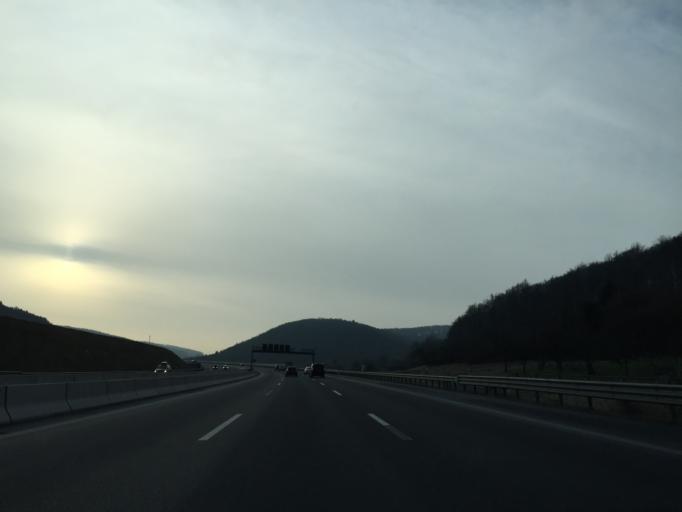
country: DE
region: Bavaria
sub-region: Regierungsbezirk Unterfranken
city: Waldaschaff
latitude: 49.9670
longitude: 9.2994
